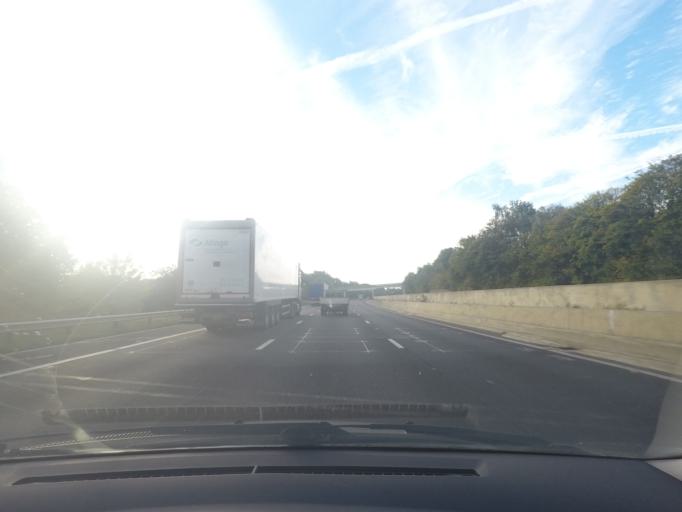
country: GB
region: England
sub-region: Barnsley
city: Darton
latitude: 53.5859
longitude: -1.5355
